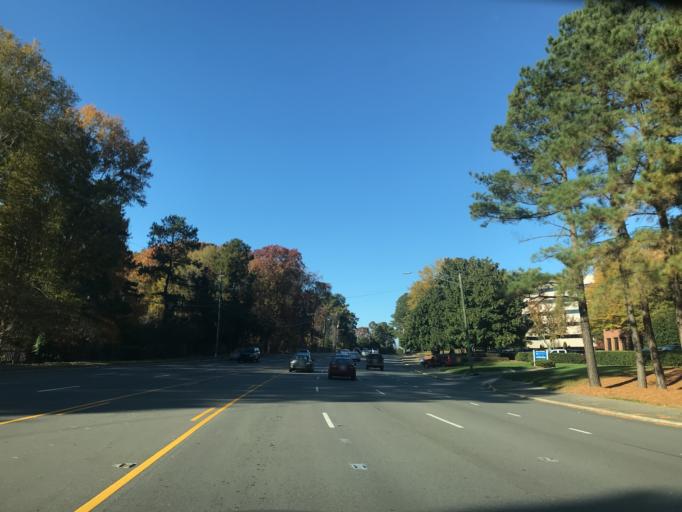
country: US
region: North Carolina
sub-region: Wake County
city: West Raleigh
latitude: 35.8450
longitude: -78.6146
